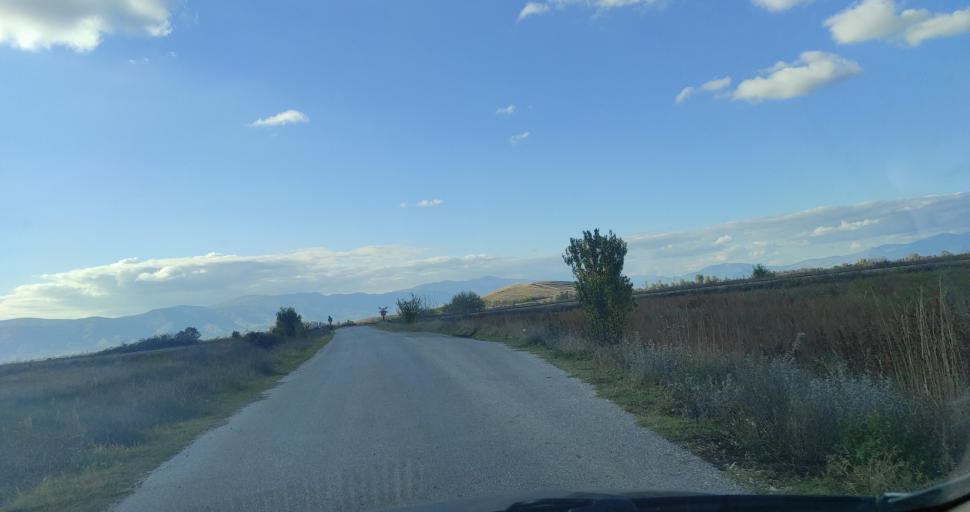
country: MK
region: Prilep
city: Topolcani
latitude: 41.2773
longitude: 21.4317
